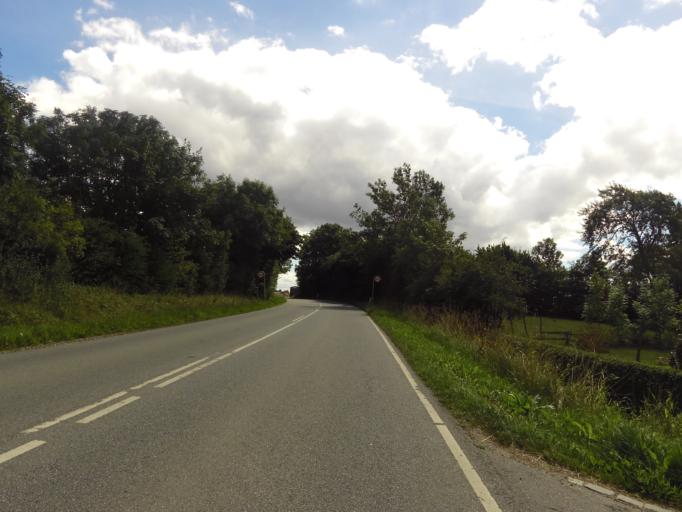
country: DK
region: South Denmark
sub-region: Haderslev Kommune
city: Haderslev
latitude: 55.2579
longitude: 9.4448
